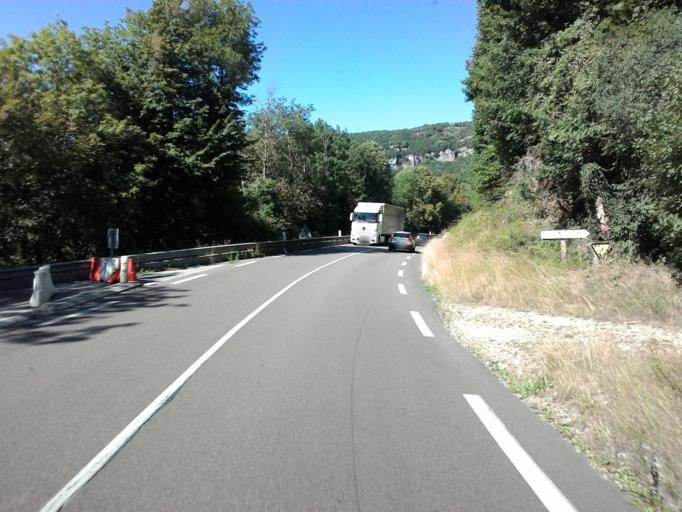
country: FR
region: Franche-Comte
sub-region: Departement du Doubs
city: Avanne-Aveney
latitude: 47.1962
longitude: 5.9684
